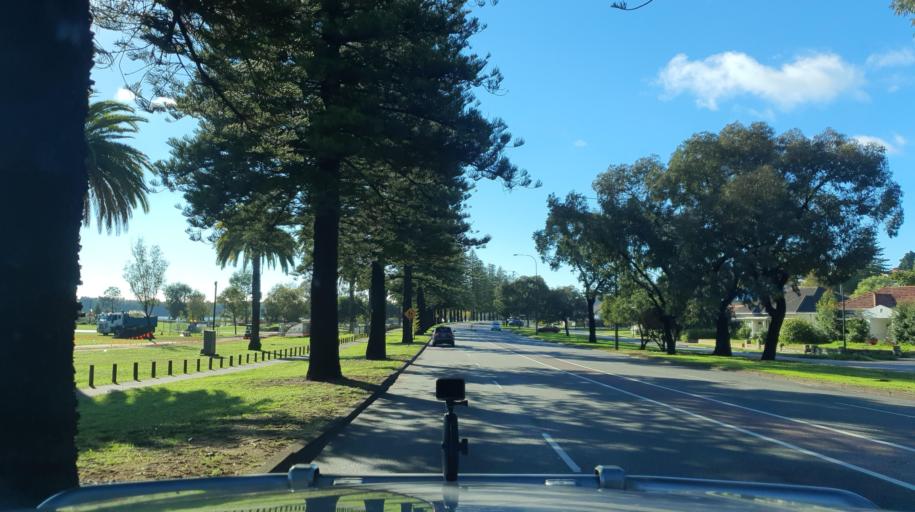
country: AU
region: Western Australia
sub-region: Cambridge
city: West Leederville
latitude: -31.9342
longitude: 115.8221
